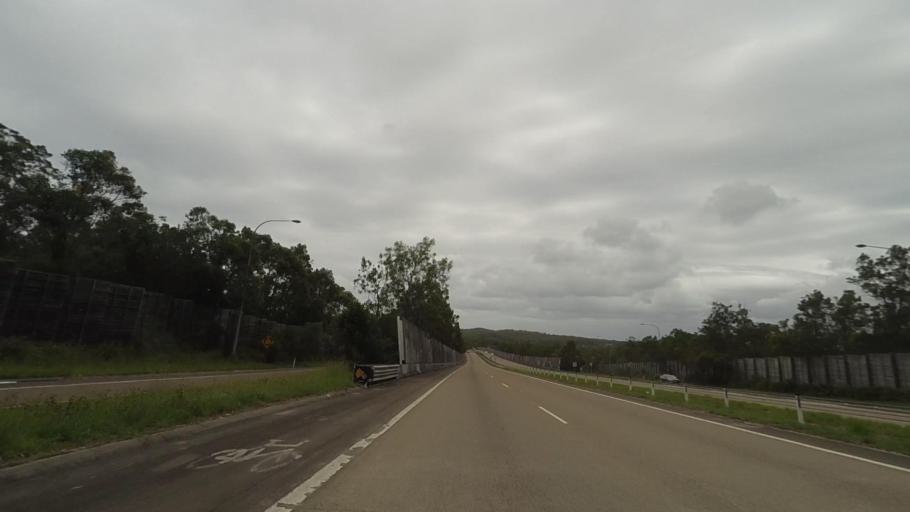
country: AU
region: New South Wales
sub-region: Lake Macquarie Shire
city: Kotara
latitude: -32.9553
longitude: 151.6811
